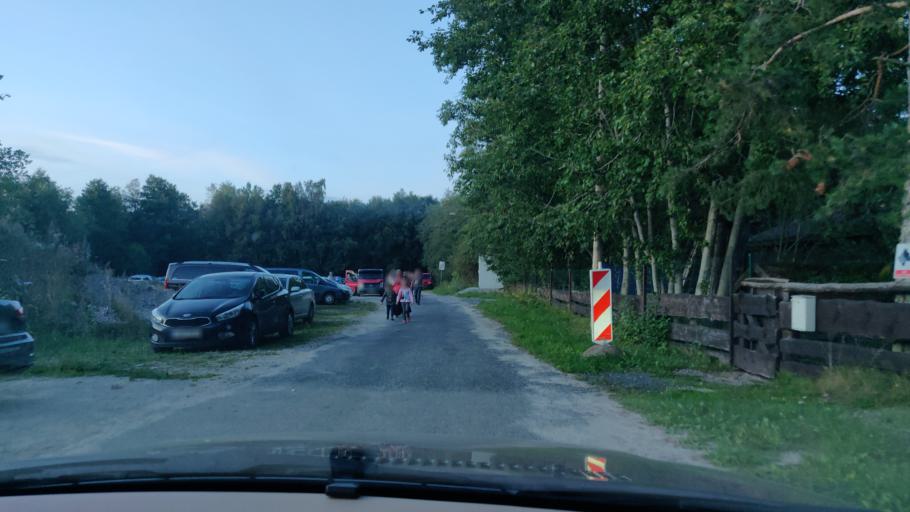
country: EE
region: Harju
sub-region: Keila linn
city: Keila
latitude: 59.3465
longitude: 24.2486
